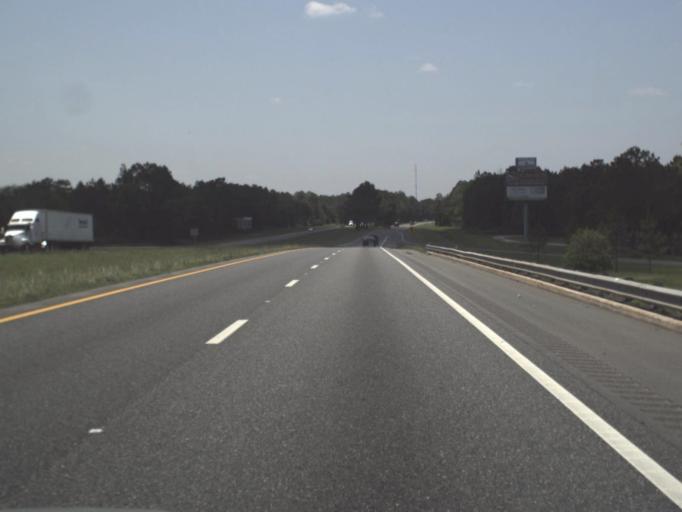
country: US
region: Florida
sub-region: Columbia County
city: Five Points
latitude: 30.2418
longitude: -82.6396
